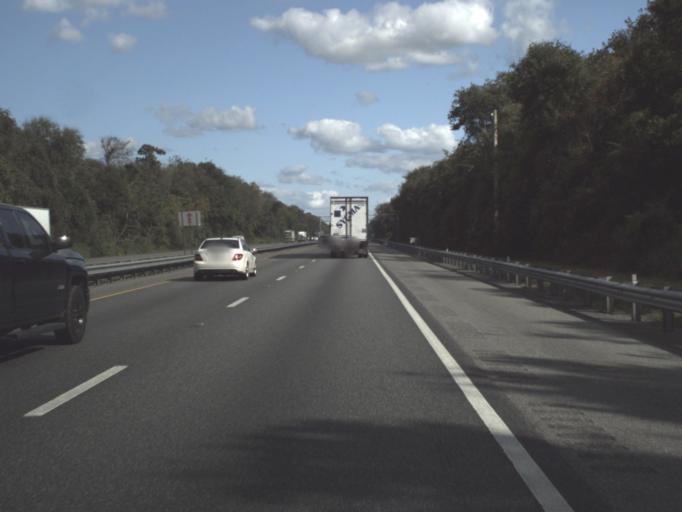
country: US
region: Florida
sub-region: Sumter County
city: Wildwood
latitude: 28.8459
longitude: -82.0730
